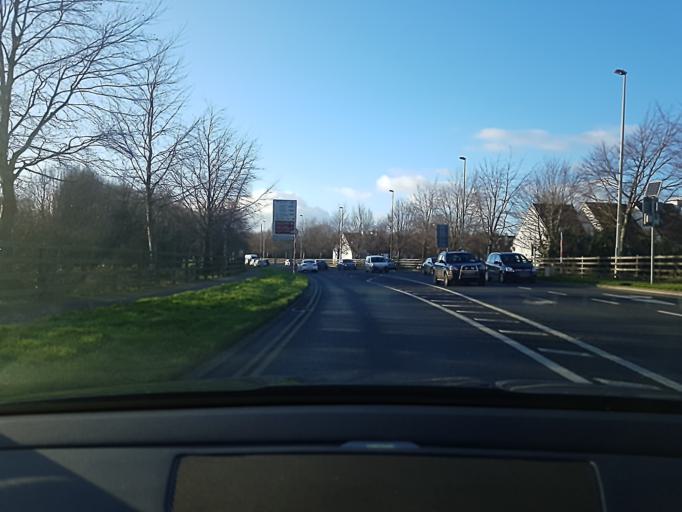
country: IE
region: Munster
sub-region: County Limerick
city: Luimneach
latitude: 52.6632
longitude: -8.6371
